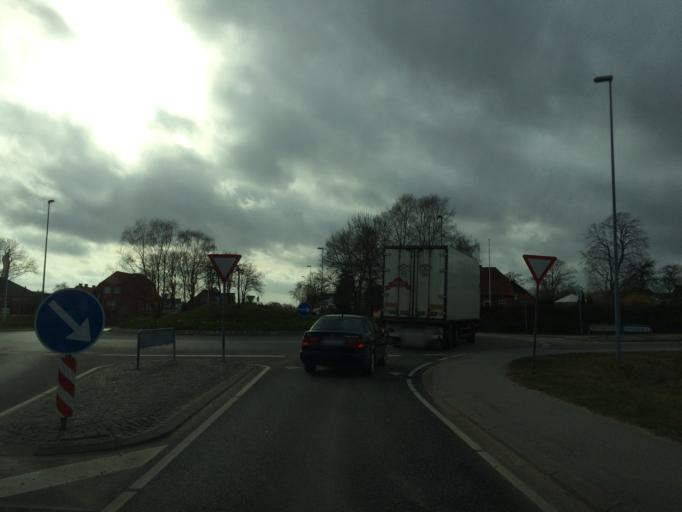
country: DK
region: Central Jutland
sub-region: Favrskov Kommune
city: Ulstrup
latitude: 56.5003
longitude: 9.7607
